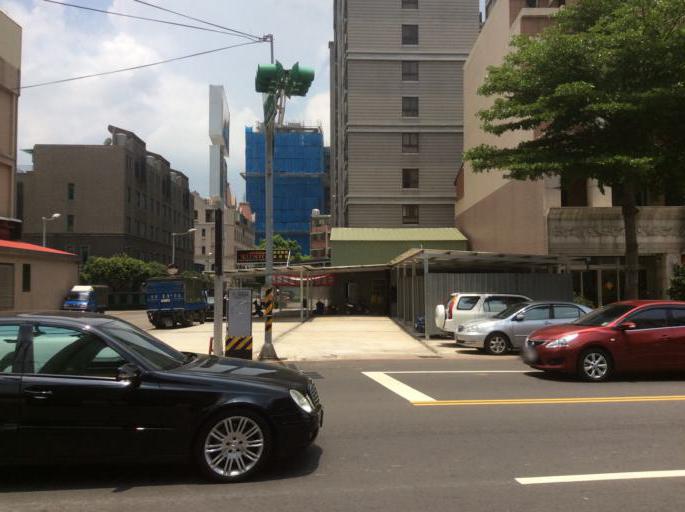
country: TW
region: Taiwan
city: Taoyuan City
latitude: 24.9612
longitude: 121.2930
